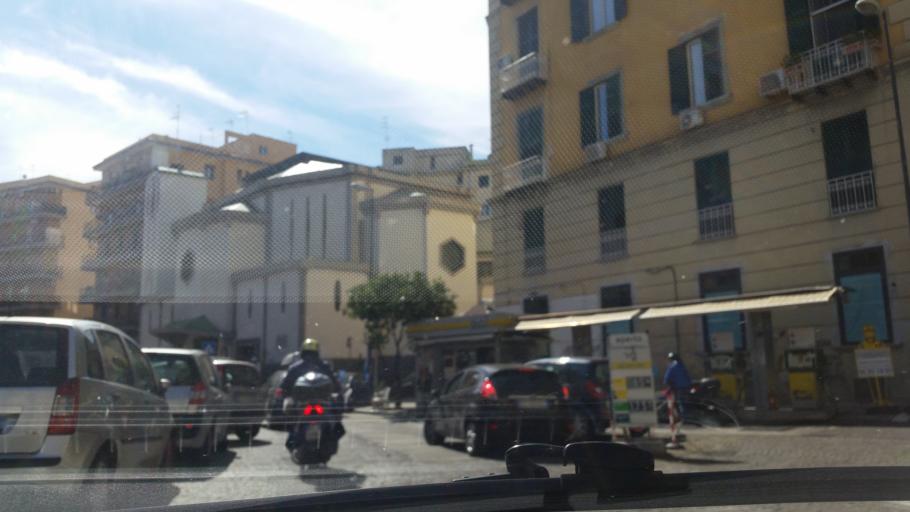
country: IT
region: Campania
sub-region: Provincia di Napoli
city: Napoli
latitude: 40.8538
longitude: 14.2356
